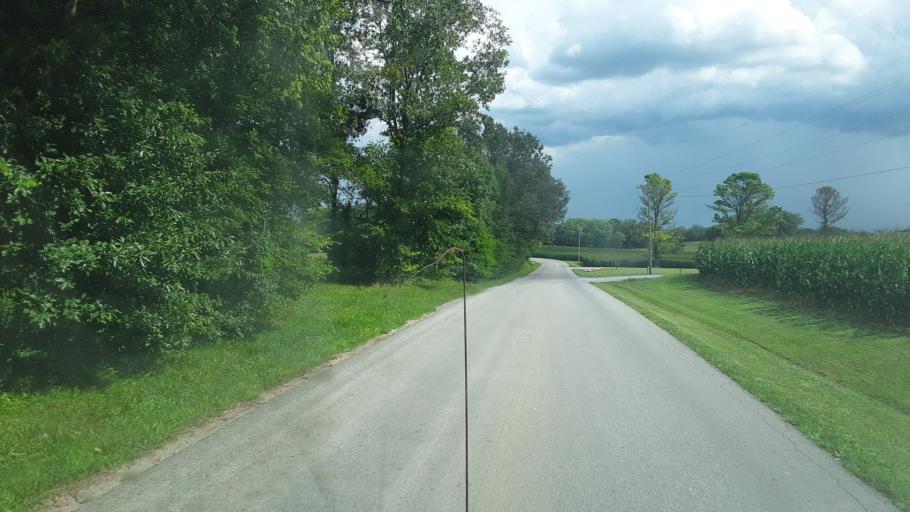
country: US
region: Kentucky
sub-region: Todd County
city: Elkton
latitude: 36.7501
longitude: -87.1709
